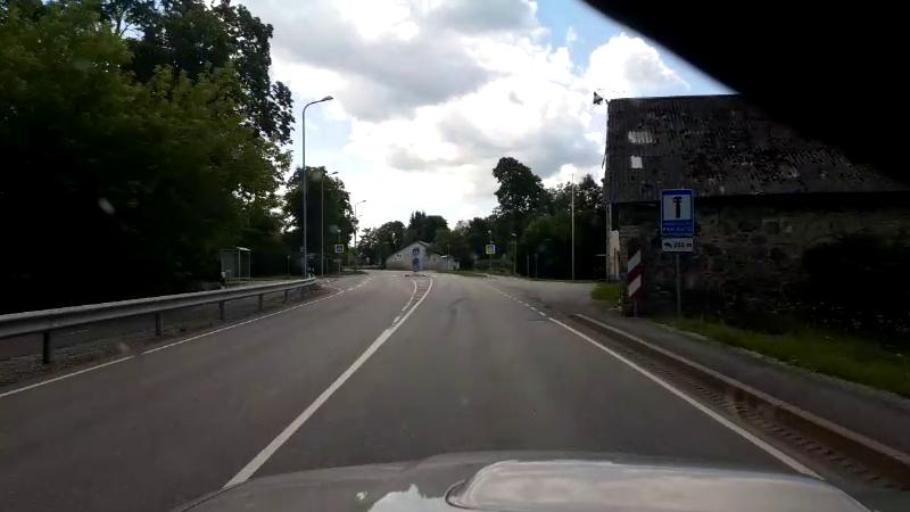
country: EE
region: Jaervamaa
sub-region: Jaerva-Jaani vald
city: Jarva-Jaani
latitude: 59.0301
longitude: 25.7029
